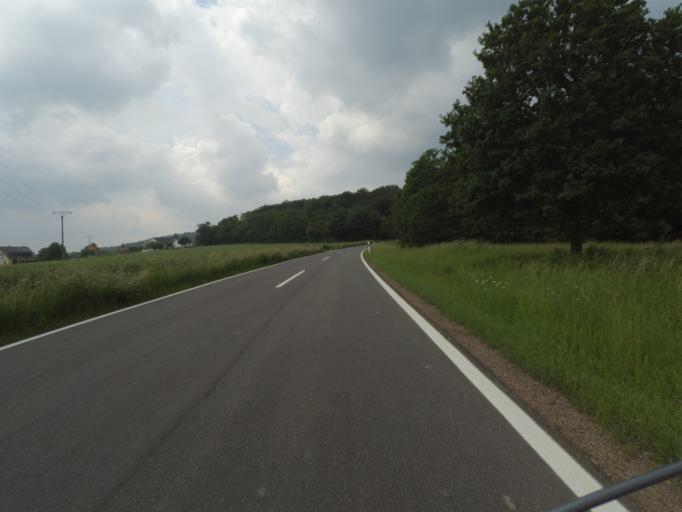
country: DE
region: Rheinland-Pfalz
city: Lutz
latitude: 50.1563
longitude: 7.3351
